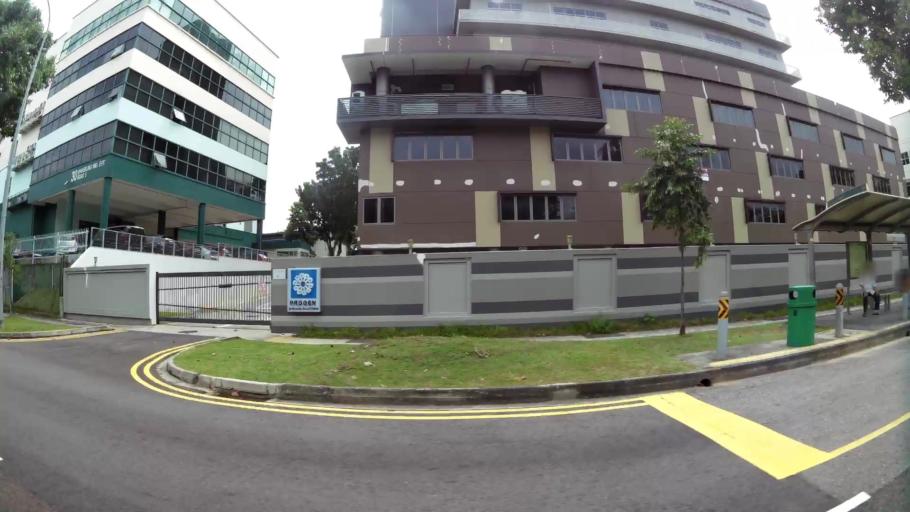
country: MY
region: Johor
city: Johor Bahru
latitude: 1.4427
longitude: 103.7829
